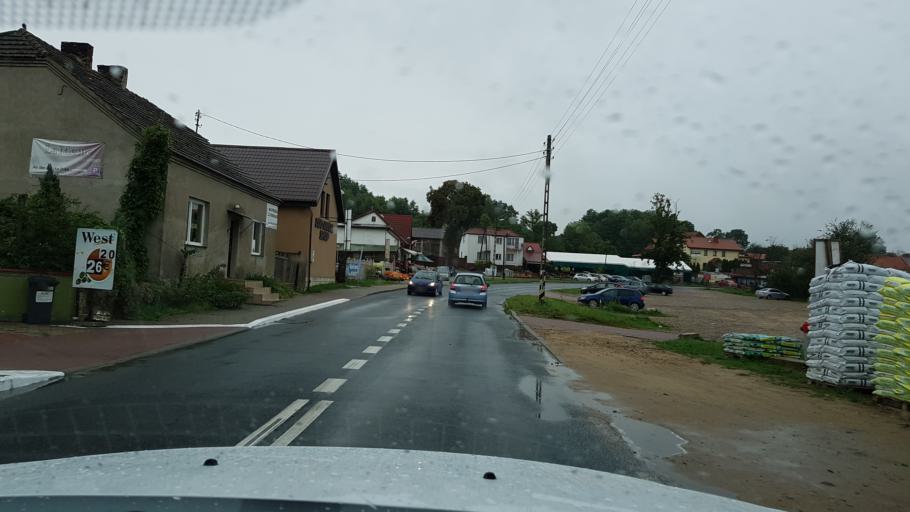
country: DE
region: Brandenburg
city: Schwedt (Oder)
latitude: 53.0323
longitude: 14.3197
